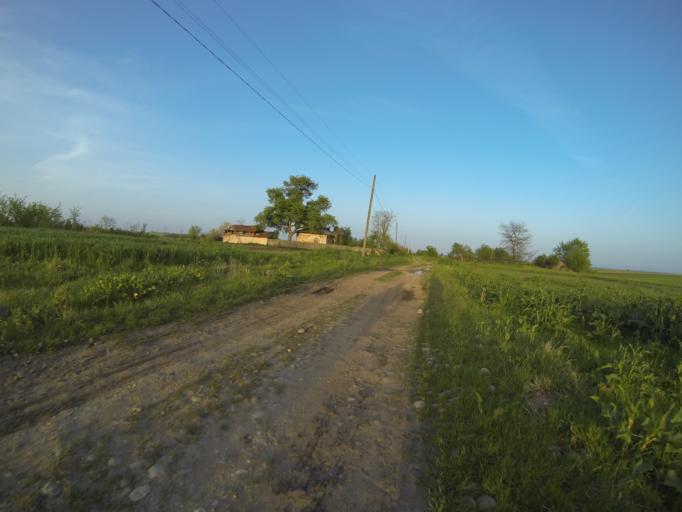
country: RO
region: Dolj
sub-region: Comuna Pielesti
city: Pielesti
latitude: 44.3623
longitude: 23.9557
